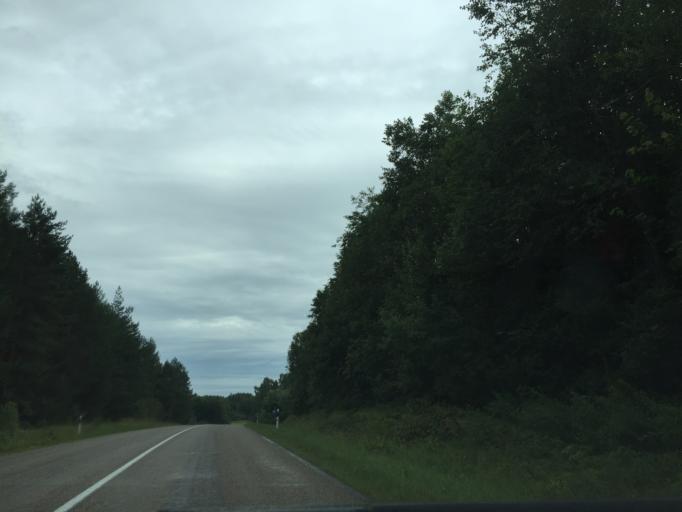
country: LV
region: Dagda
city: Dagda
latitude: 56.1881
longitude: 27.3535
